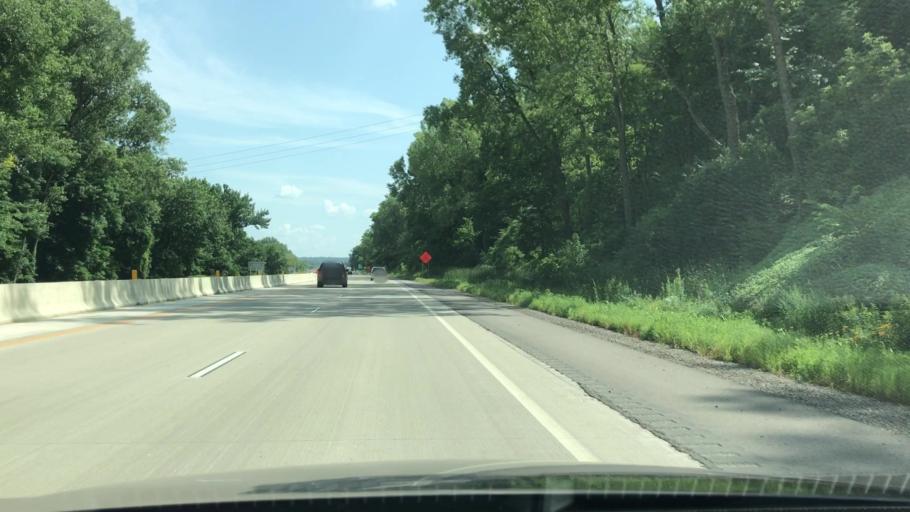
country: US
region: Minnesota
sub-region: Nicollet County
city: North Mankato
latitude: 44.2094
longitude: -94.0259
